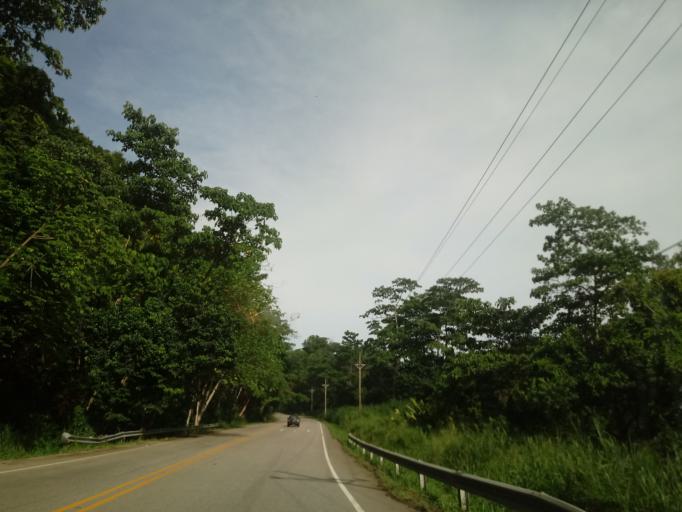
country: CR
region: San Jose
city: Daniel Flores
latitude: 9.2029
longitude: -83.7923
